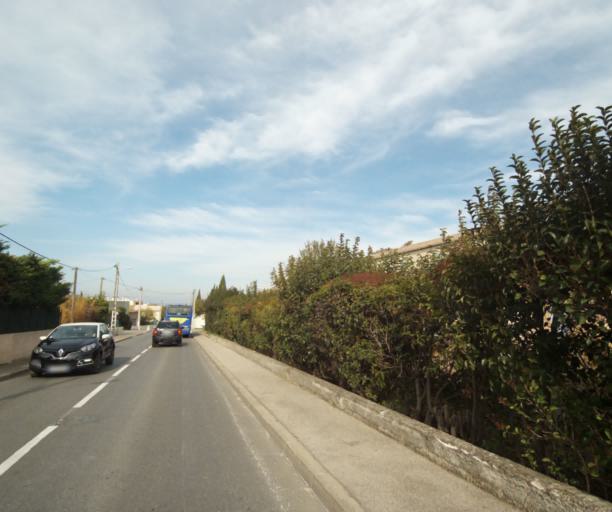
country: FR
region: Provence-Alpes-Cote d'Azur
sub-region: Departement des Bouches-du-Rhone
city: Gignac-la-Nerthe
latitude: 43.3916
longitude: 5.2324
